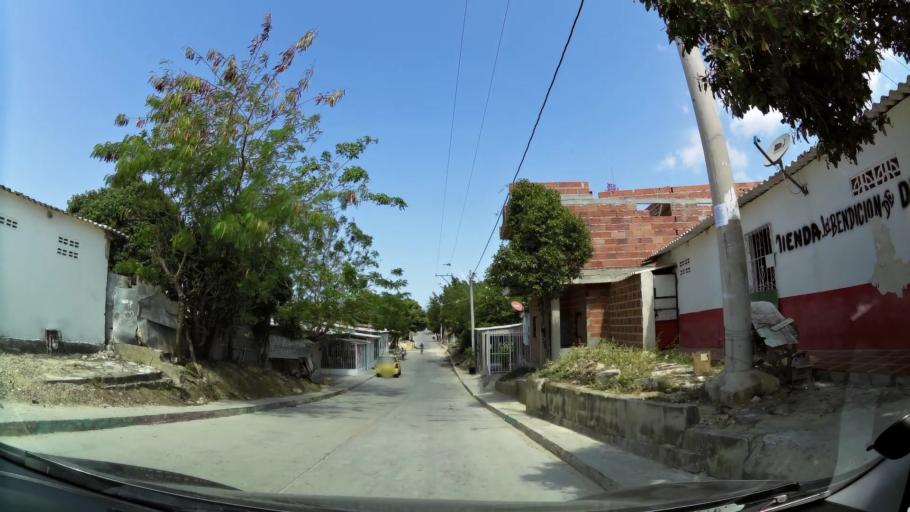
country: CO
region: Atlantico
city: Barranquilla
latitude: 10.9624
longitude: -74.8263
